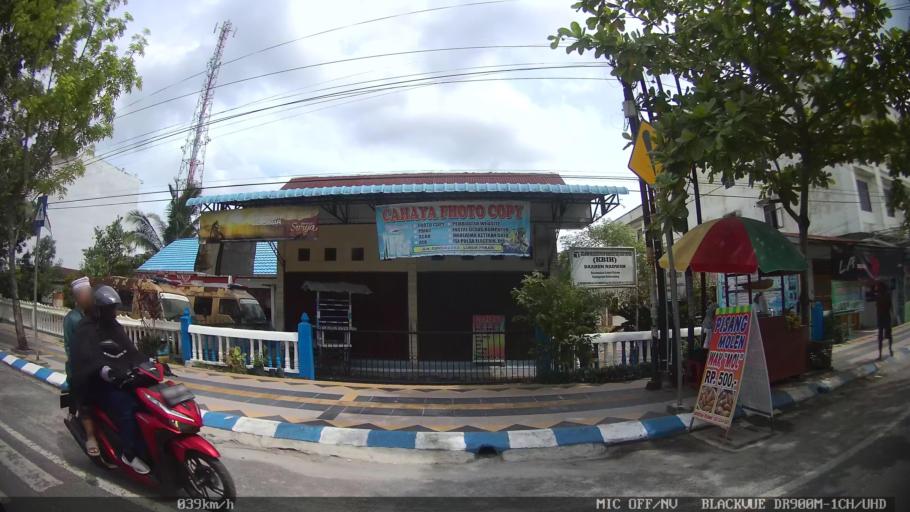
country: ID
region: North Sumatra
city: Percut
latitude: 3.5595
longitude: 98.8705
